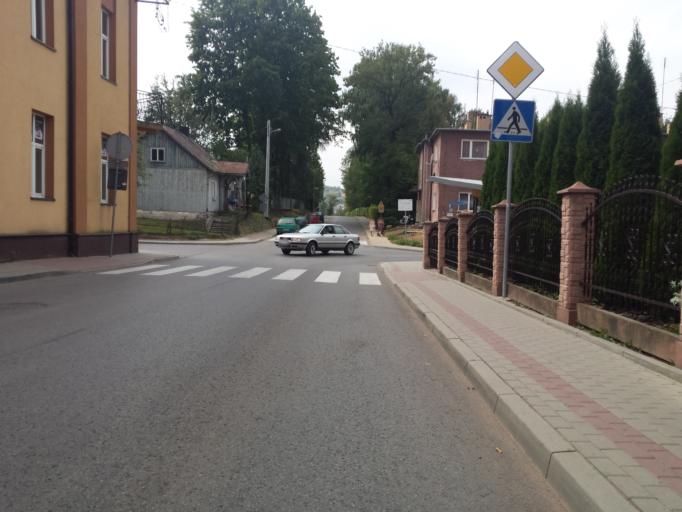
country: PL
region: Subcarpathian Voivodeship
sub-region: Powiat rzeszowski
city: Dynow
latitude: 49.8147
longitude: 22.2315
